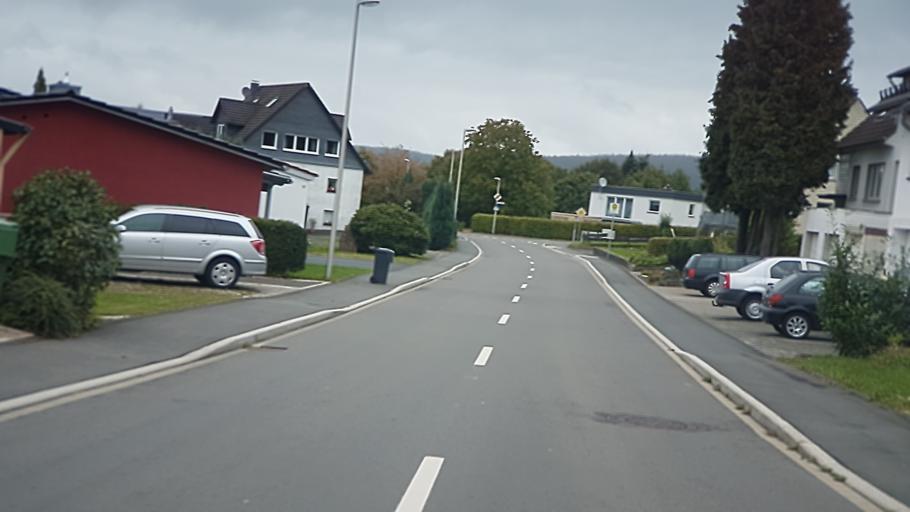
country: DE
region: North Rhine-Westphalia
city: Meinerzhagen
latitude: 51.1144
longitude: 7.6473
